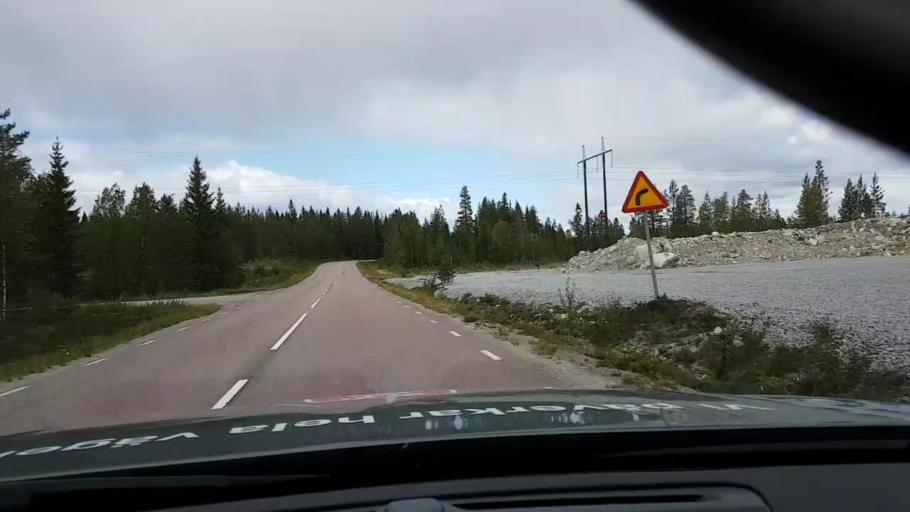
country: SE
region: Vaesterbotten
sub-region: Asele Kommun
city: Asele
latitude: 63.8875
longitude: 17.3504
